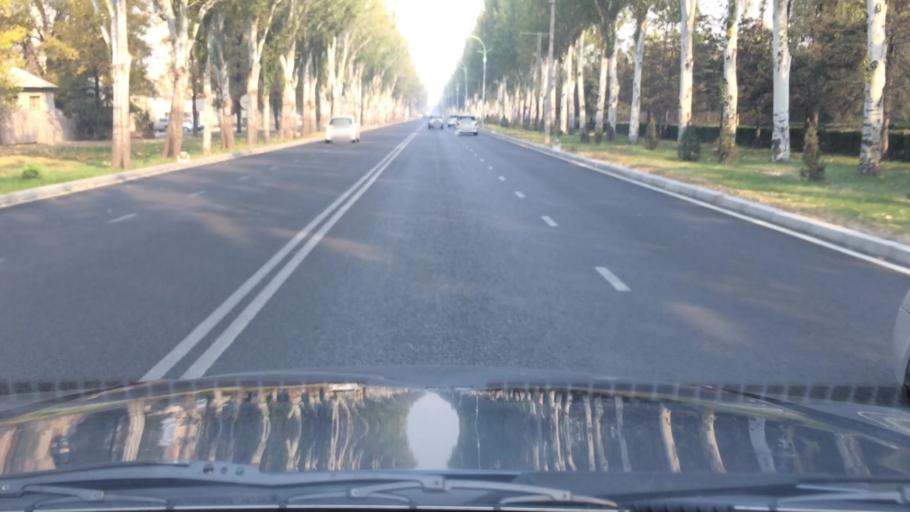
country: KG
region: Chuy
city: Bishkek
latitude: 42.8339
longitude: 74.5855
